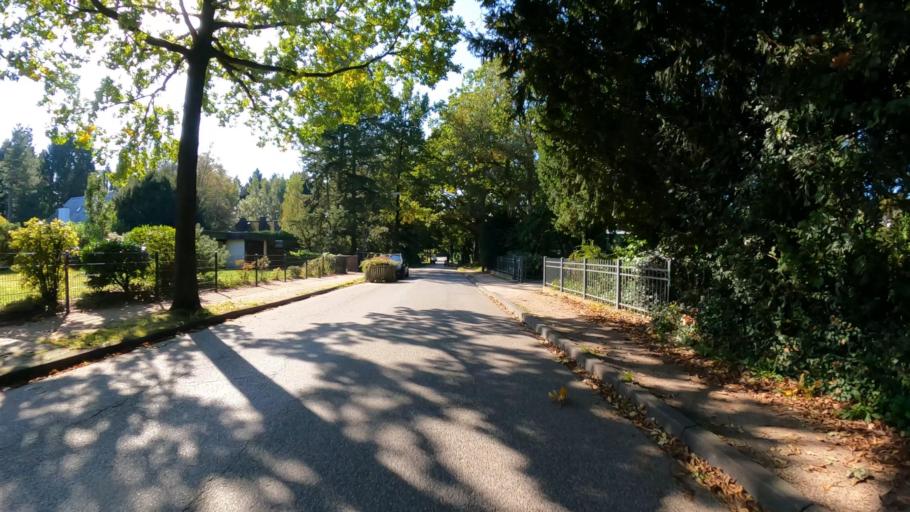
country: DE
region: Schleswig-Holstein
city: Ahrensburg
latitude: 53.6597
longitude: 10.1868
